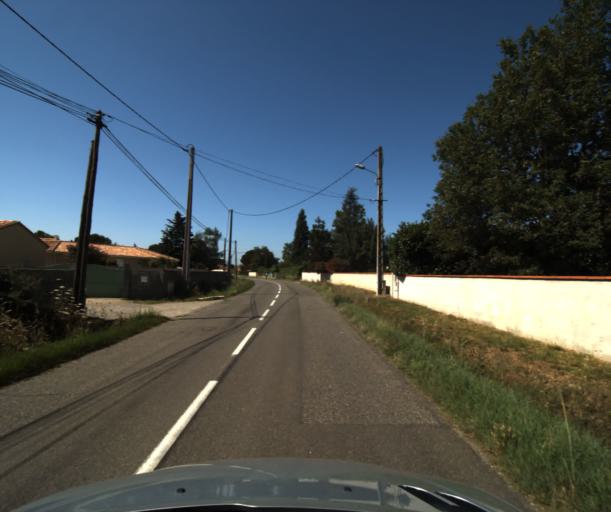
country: FR
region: Midi-Pyrenees
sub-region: Departement de la Haute-Garonne
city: Saubens
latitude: 43.4916
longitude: 1.3526
